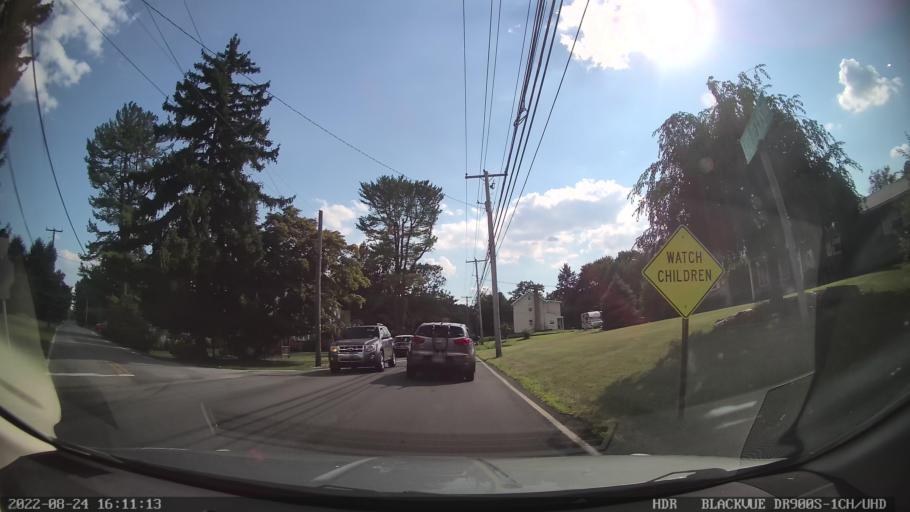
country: US
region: Pennsylvania
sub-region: Lehigh County
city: Dorneyville
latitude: 40.5614
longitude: -75.5329
